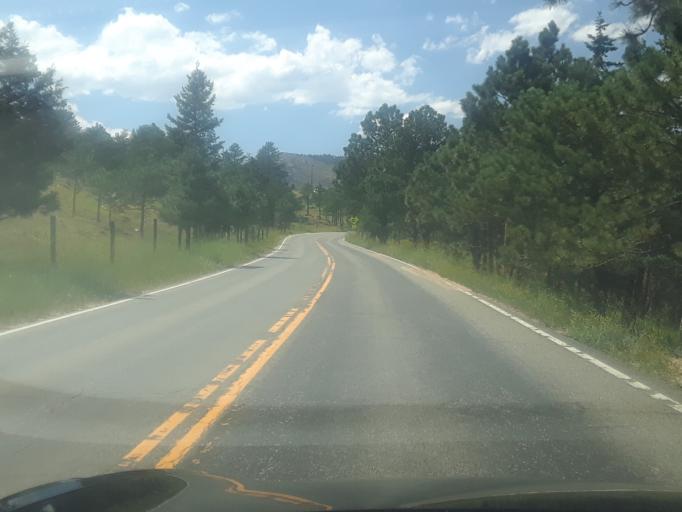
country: US
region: Colorado
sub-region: Boulder County
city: Boulder
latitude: 40.0542
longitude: -105.3595
